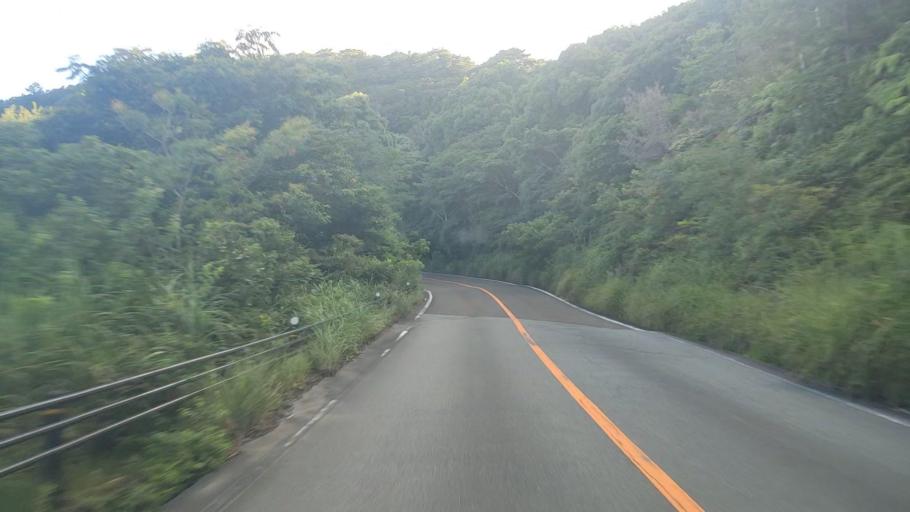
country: JP
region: Mie
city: Toba
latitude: 34.3850
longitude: 136.8608
